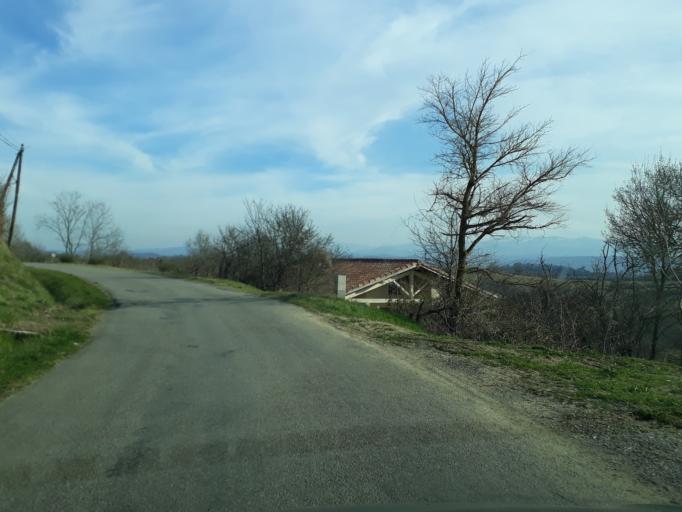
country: FR
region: Midi-Pyrenees
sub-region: Departement de la Haute-Garonne
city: Montesquieu-Volvestre
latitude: 43.1802
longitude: 1.3148
